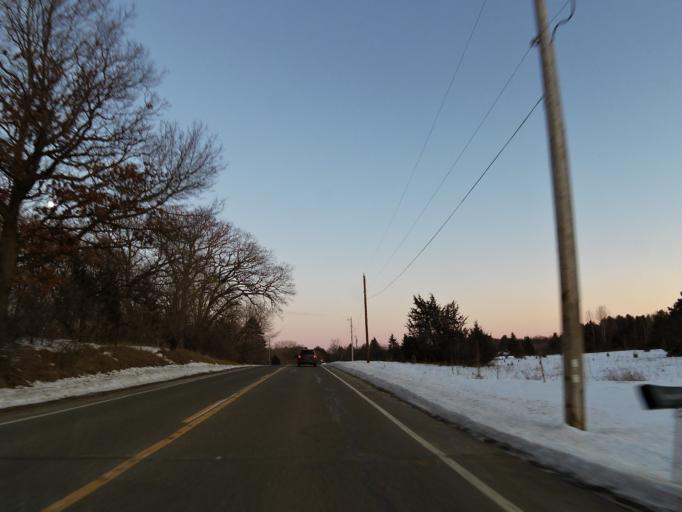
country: US
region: Minnesota
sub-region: Washington County
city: Grant
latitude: 45.0821
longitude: -92.9039
